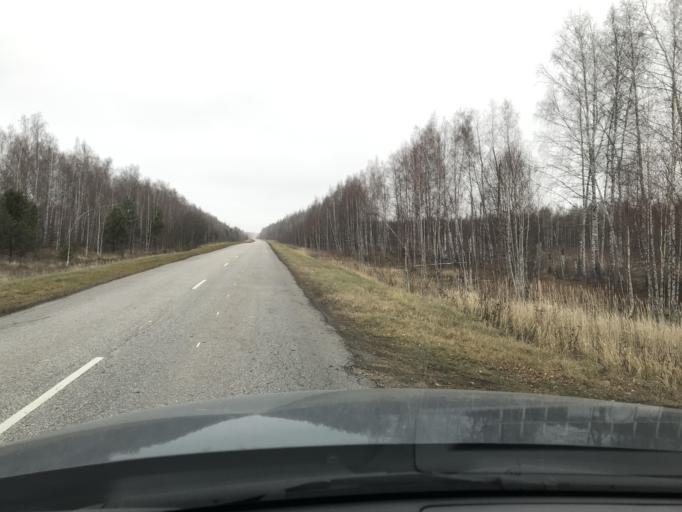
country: RU
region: Penza
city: Zemetchino
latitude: 53.6860
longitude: 42.6359
